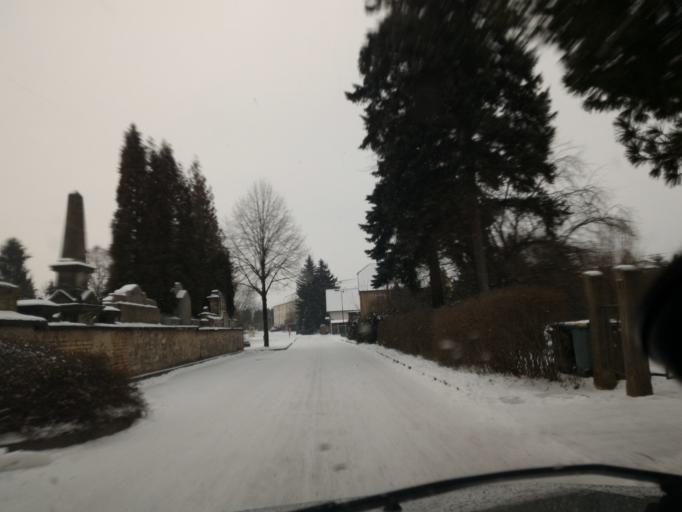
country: DE
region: Saxony
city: Grossschonau
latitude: 50.8897
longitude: 14.6618
